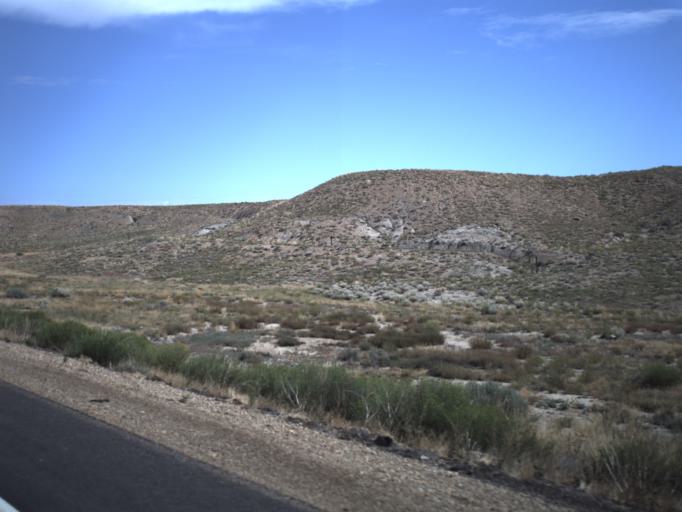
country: US
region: Utah
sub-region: Carbon County
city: East Carbon City
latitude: 39.4732
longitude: -110.5015
